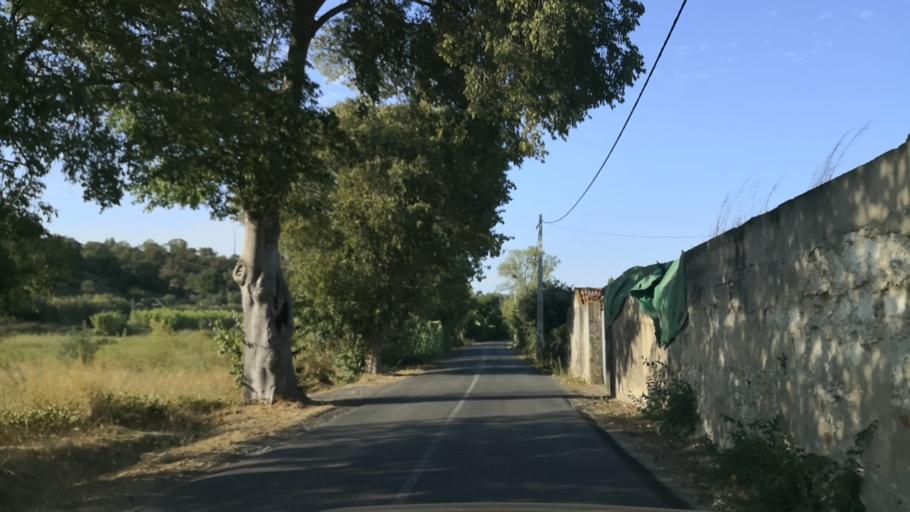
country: PT
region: Santarem
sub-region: Santarem
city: Santarem
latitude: 39.2546
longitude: -8.6714
